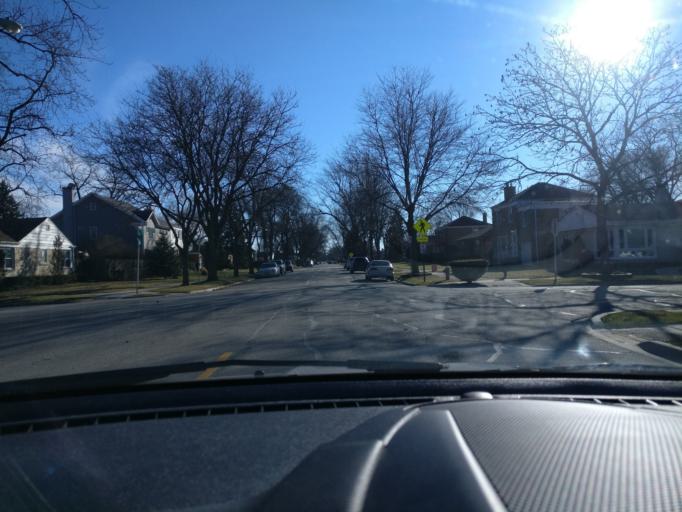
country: US
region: Illinois
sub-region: Cook County
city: Skokie
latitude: 42.0383
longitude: -87.7569
